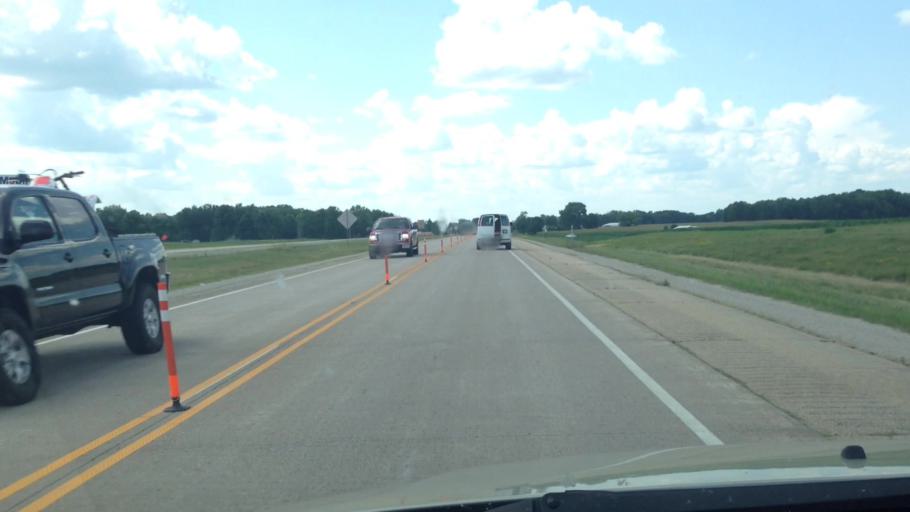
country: US
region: Wisconsin
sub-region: Brown County
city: Pulaski
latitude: 44.6922
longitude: -88.3344
